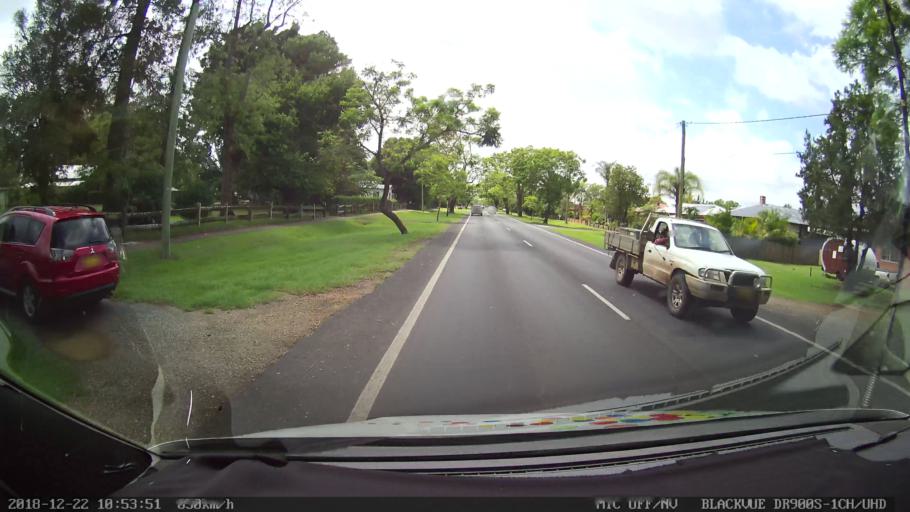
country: AU
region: New South Wales
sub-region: Clarence Valley
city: South Grafton
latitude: -29.6983
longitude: 152.9199
